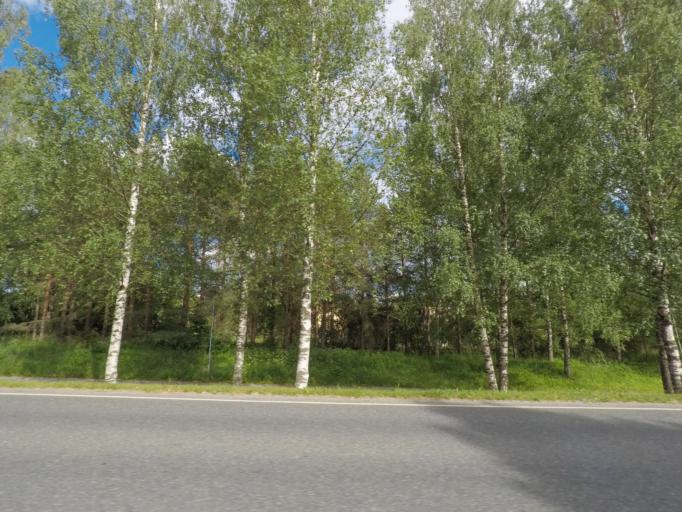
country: FI
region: Paijanne Tavastia
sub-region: Lahti
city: Lahti
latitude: 60.9632
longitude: 25.6237
